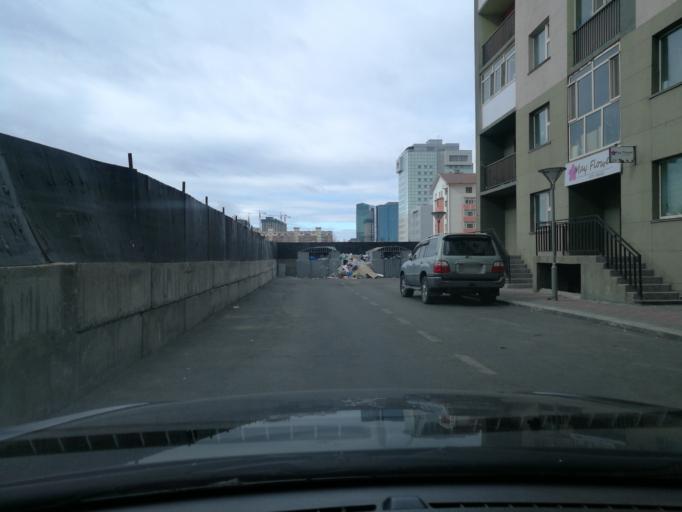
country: MN
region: Ulaanbaatar
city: Ulaanbaatar
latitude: 47.9031
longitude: 106.9266
